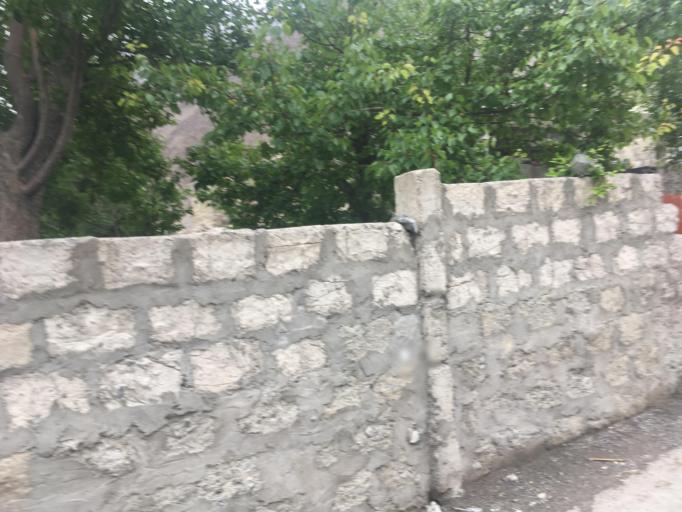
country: PK
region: Gilgit-Baltistan
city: Skardu
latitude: 35.2660
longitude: 75.6341
